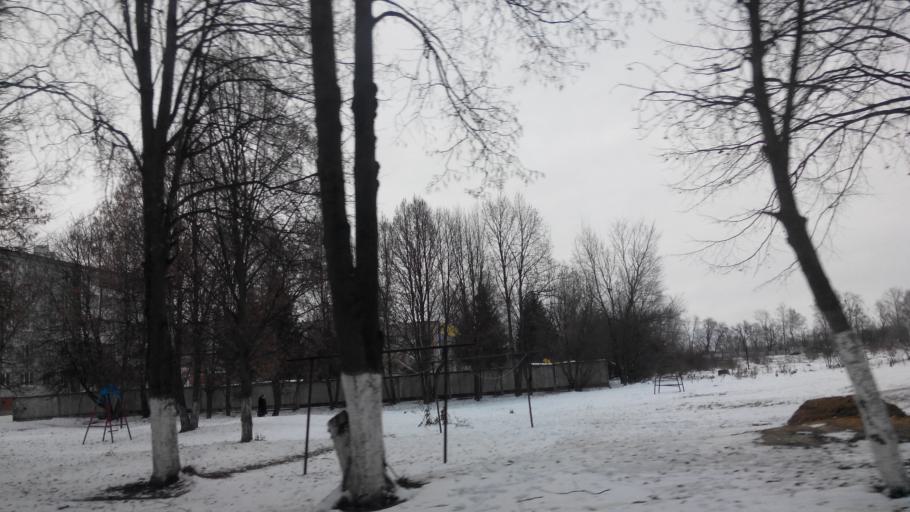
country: RU
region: Tula
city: Podlesnyy
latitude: 53.9679
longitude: 38.2864
